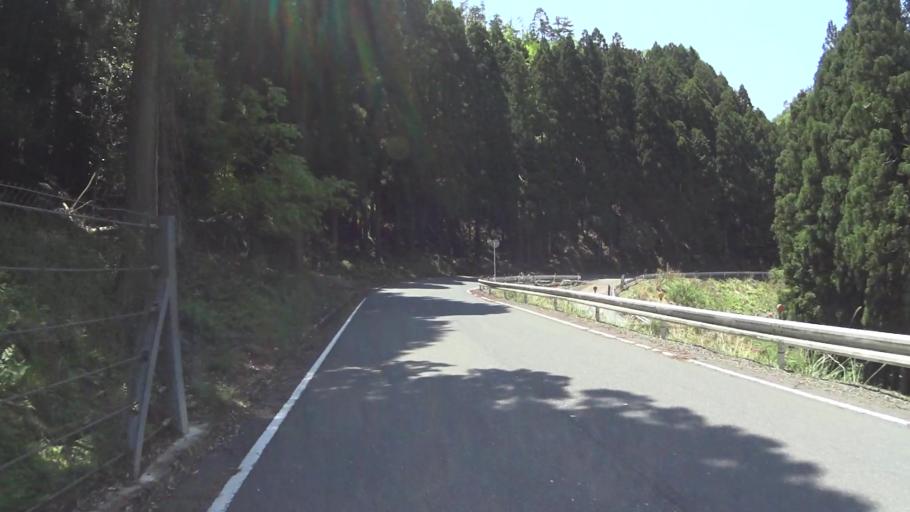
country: JP
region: Kyoto
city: Kameoka
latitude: 35.0882
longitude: 135.5831
